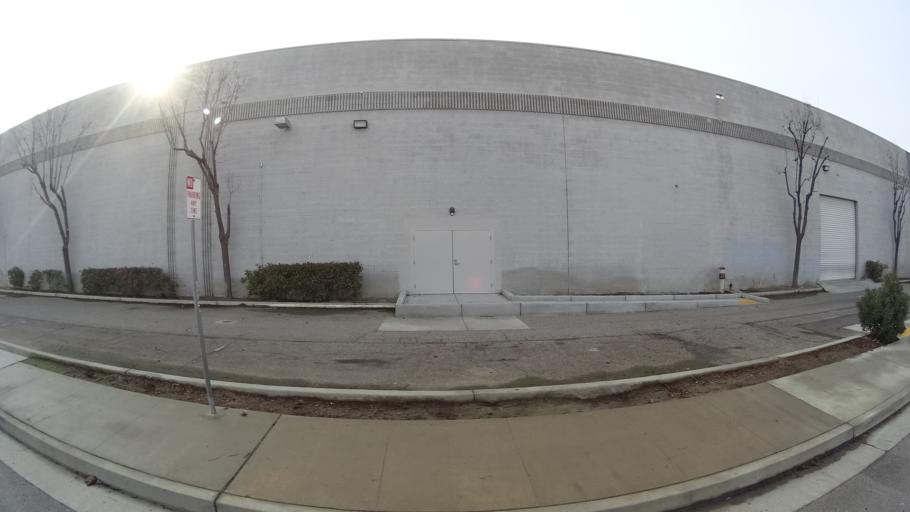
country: US
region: California
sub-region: Kern County
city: Bakersfield
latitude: 35.3894
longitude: -119.0395
